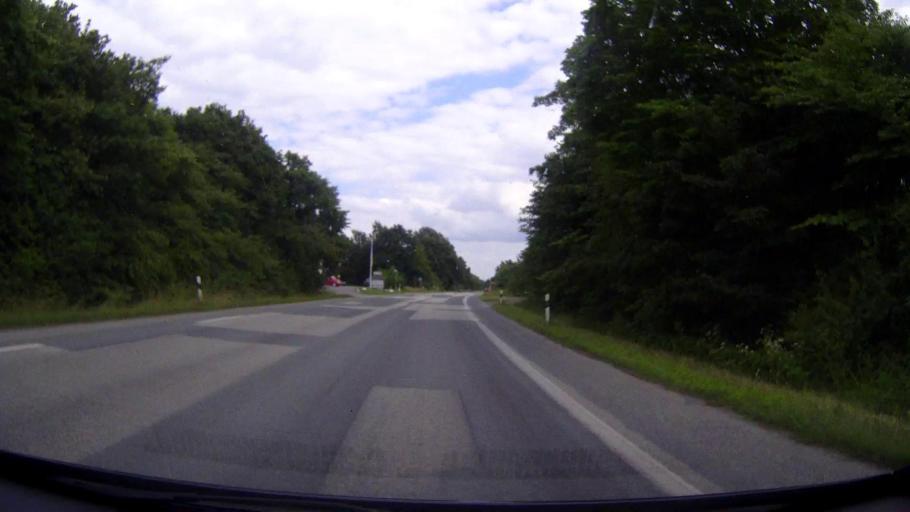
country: DE
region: Schleswig-Holstein
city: Badendorf
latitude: 53.8974
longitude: 10.5939
